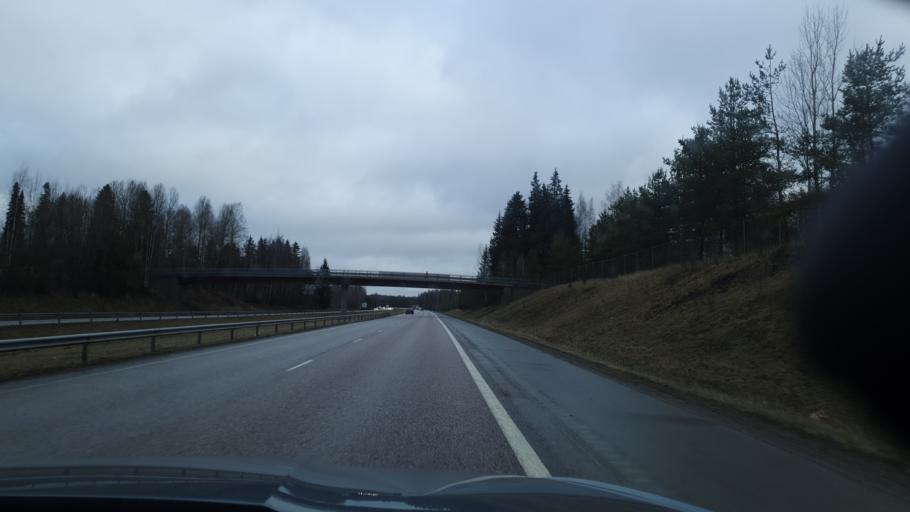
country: FI
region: Uusimaa
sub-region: Helsinki
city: Hyvinge
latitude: 60.6312
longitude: 24.8100
